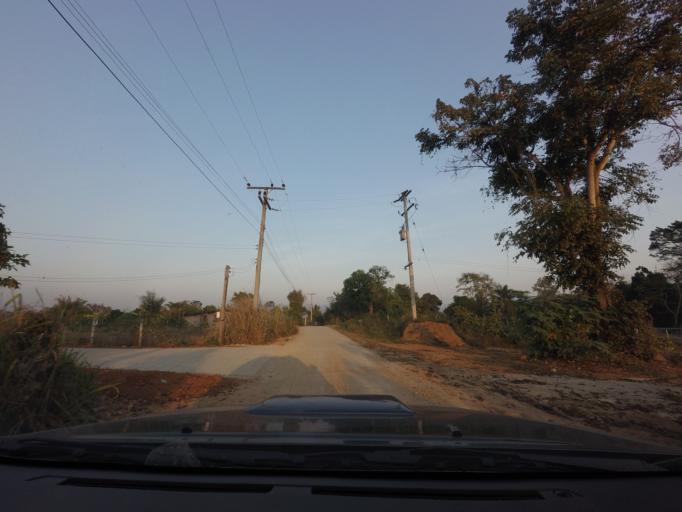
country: TH
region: Chiang Mai
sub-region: Amphoe Chiang Dao
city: Chiang Dao
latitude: 19.3681
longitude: 98.9533
